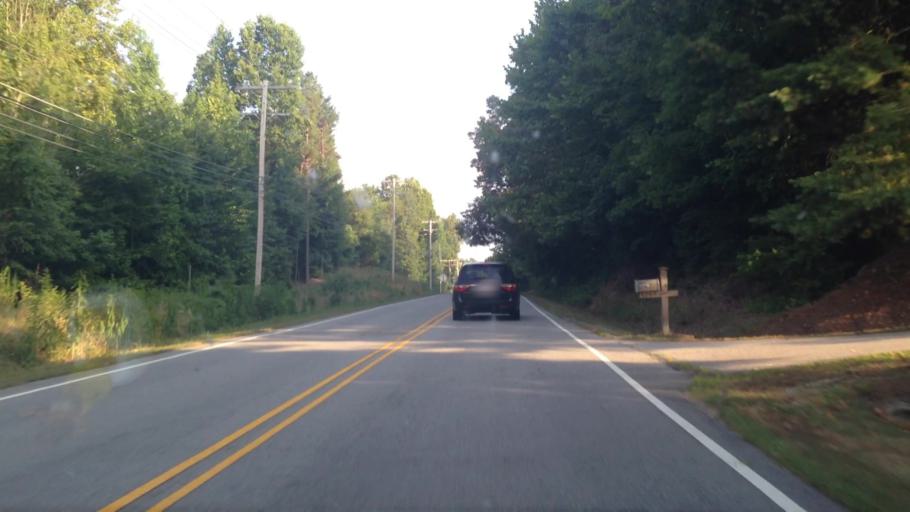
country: US
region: North Carolina
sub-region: Davidson County
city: Thomasville
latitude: 35.9461
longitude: -80.0757
